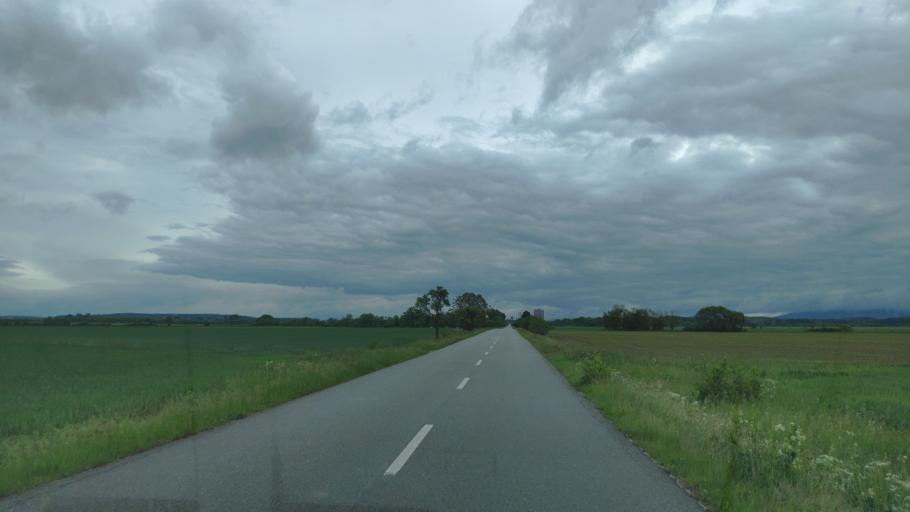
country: SK
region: Kosicky
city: Moldava nad Bodvou
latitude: 48.5783
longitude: 21.1252
